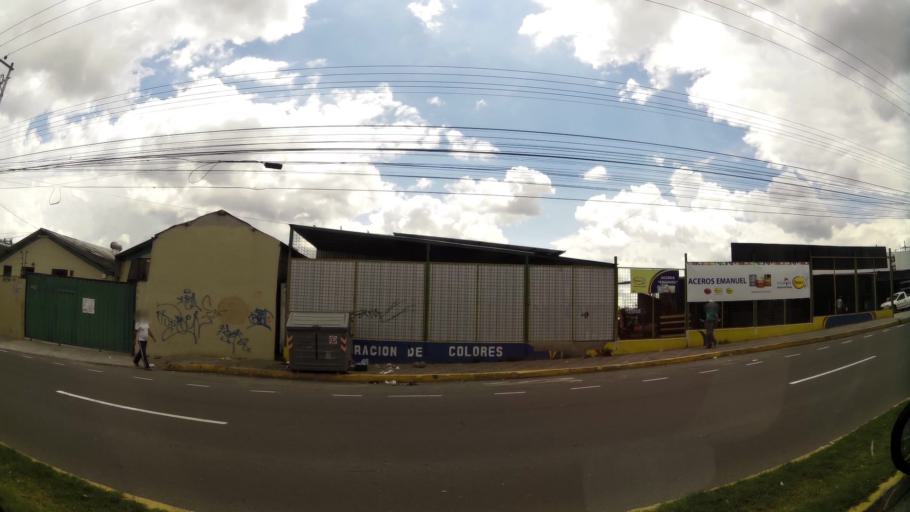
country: EC
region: Pichincha
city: Quito
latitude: -0.1018
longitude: -78.4490
